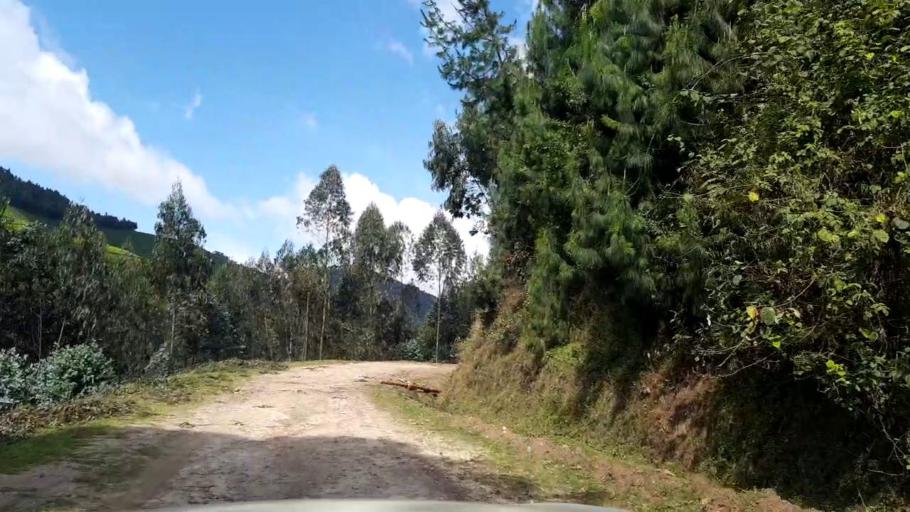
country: RW
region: Western Province
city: Kibuye
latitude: -1.8814
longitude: 29.4693
